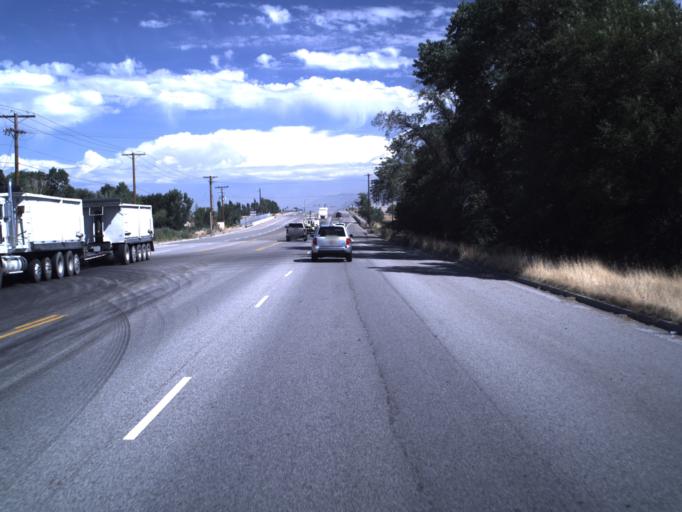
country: US
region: Utah
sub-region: Weber County
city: Marriott-Slaterville
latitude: 41.2390
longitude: -112.0254
